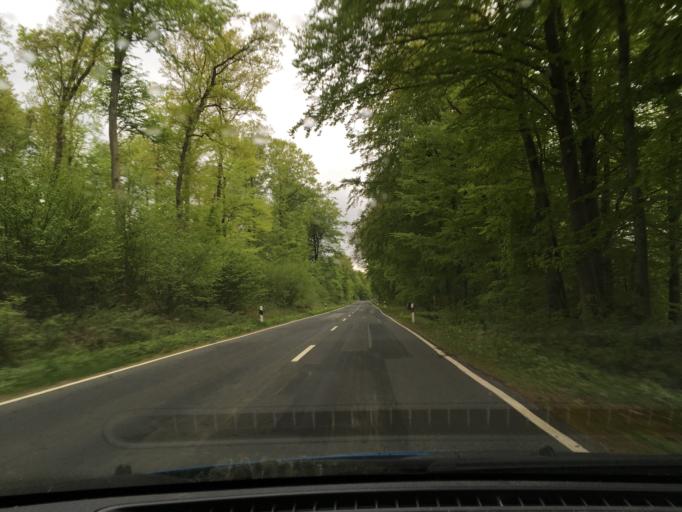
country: DE
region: Lower Saxony
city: Heinade
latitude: 51.7969
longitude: 9.6440
